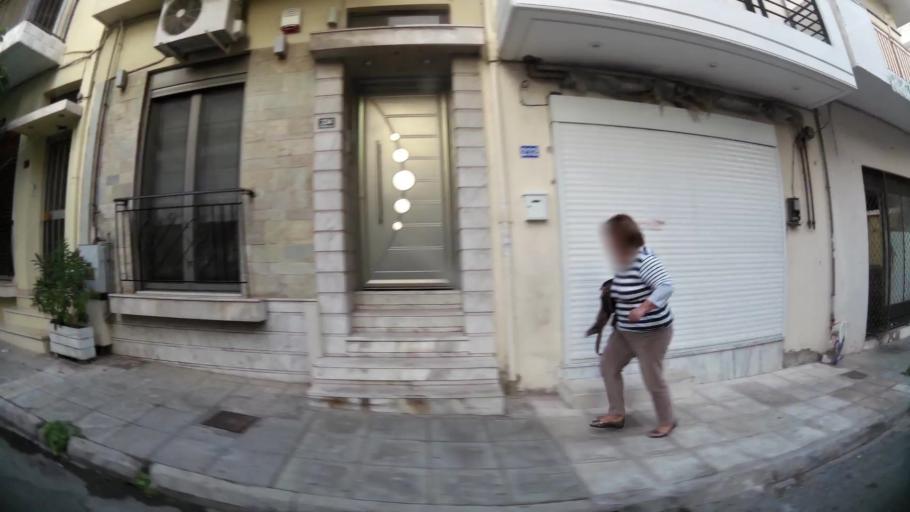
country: GR
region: Attica
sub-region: Nomos Piraios
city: Nikaia
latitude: 37.9735
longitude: 23.6440
